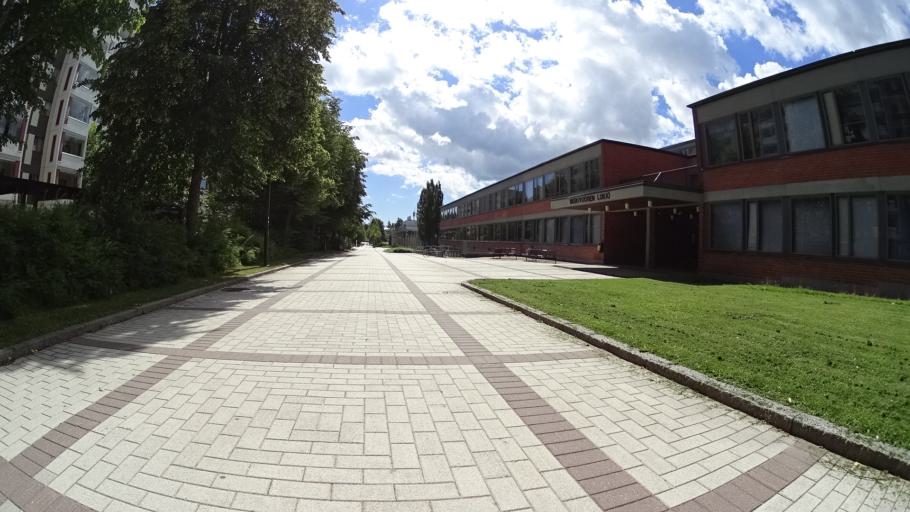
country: FI
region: Uusimaa
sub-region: Helsinki
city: Teekkarikylae
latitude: 60.2666
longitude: 24.8519
